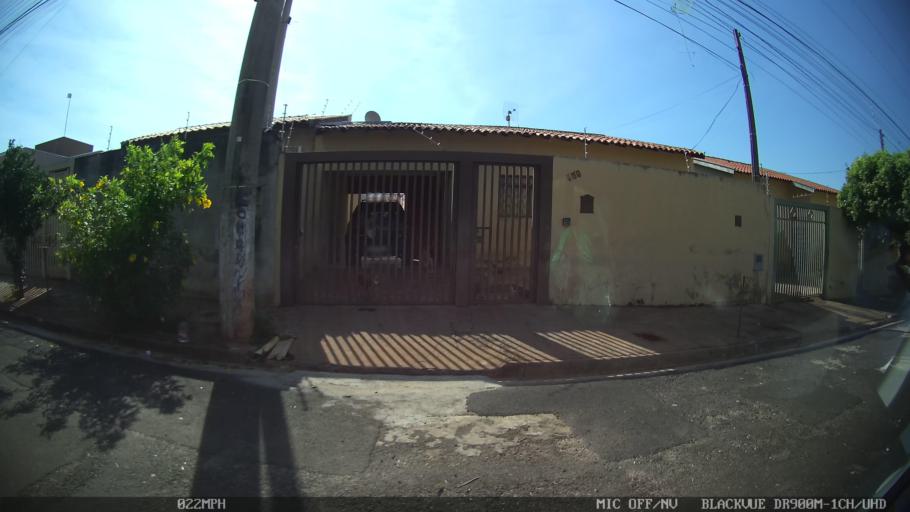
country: BR
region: Sao Paulo
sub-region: Sao Jose Do Rio Preto
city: Sao Jose do Rio Preto
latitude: -20.7882
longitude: -49.4373
